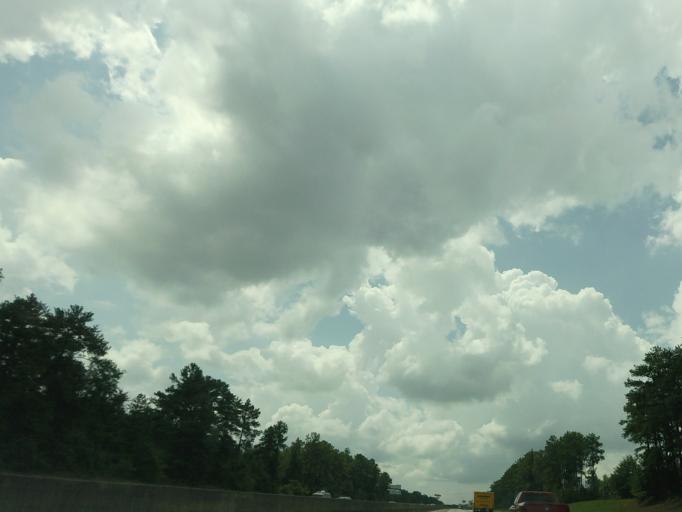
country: US
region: Georgia
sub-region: Peach County
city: Byron
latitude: 32.6900
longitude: -83.7392
